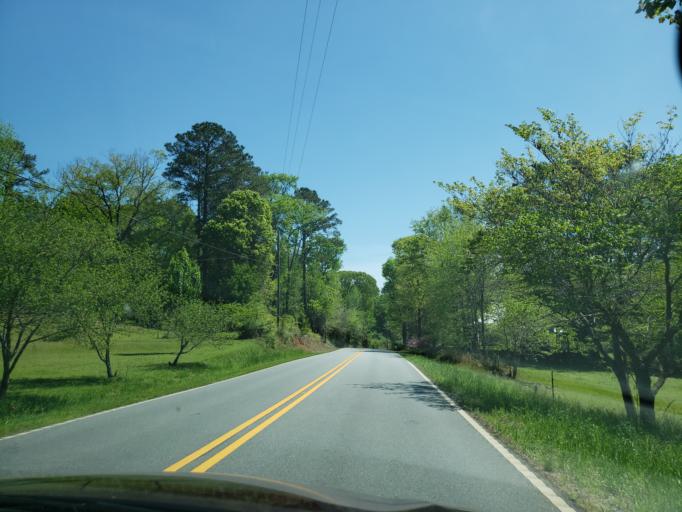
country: US
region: Alabama
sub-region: Tallapoosa County
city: Dadeville
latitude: 32.7024
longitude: -85.7530
